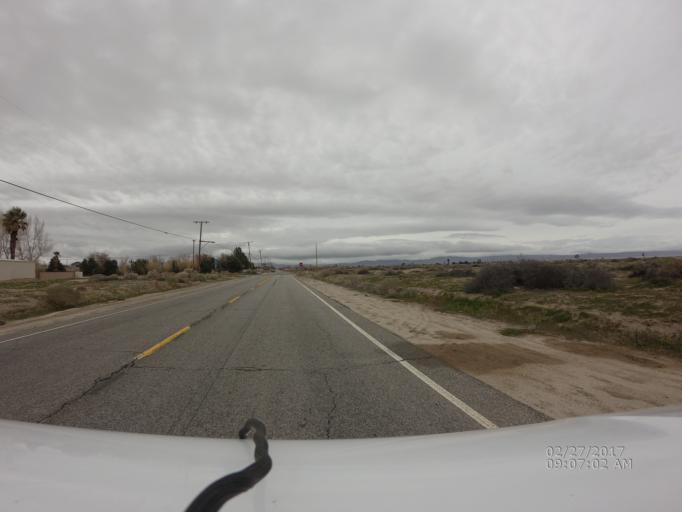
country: US
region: California
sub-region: Los Angeles County
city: Lancaster
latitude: 34.7197
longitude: -118.0772
